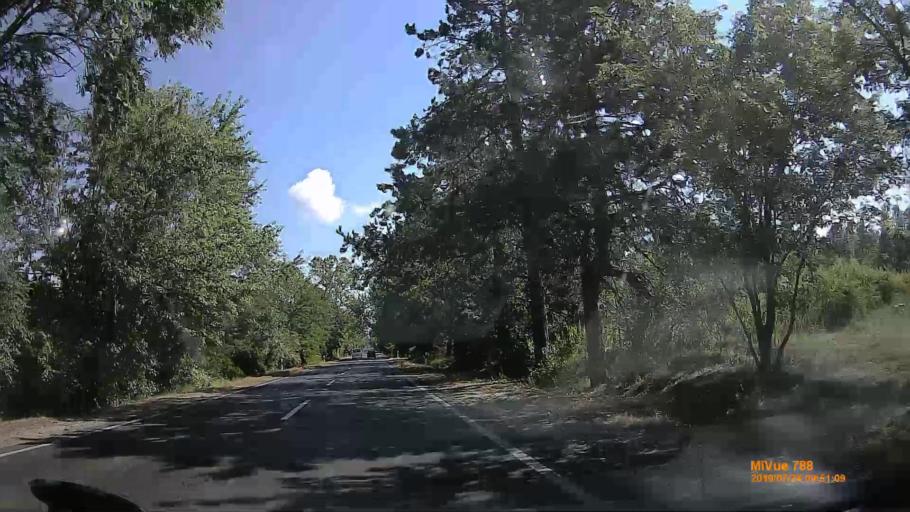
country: HU
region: Szabolcs-Szatmar-Bereg
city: Vaja
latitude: 48.0283
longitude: 22.1635
